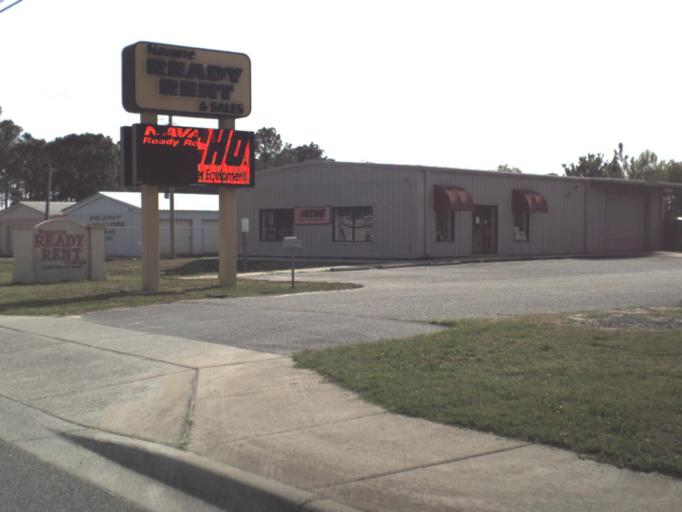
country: US
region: Florida
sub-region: Santa Rosa County
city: Navarre
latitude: 30.4137
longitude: -86.8696
